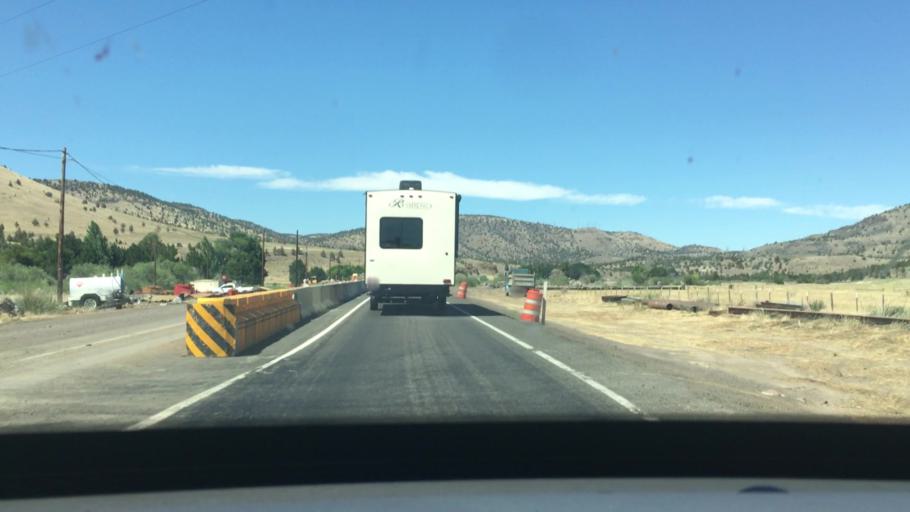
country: US
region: Oregon
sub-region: Jefferson County
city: Madras
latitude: 44.8101
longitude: -120.9330
